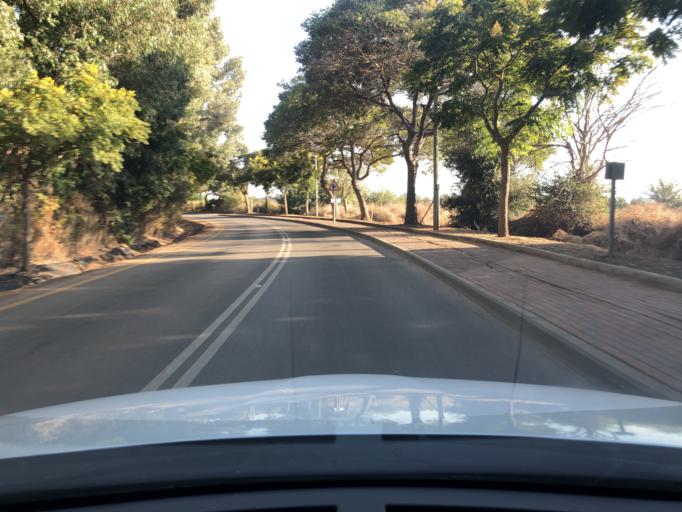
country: IL
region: Central District
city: Hod HaSharon
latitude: 32.1361
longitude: 34.9075
